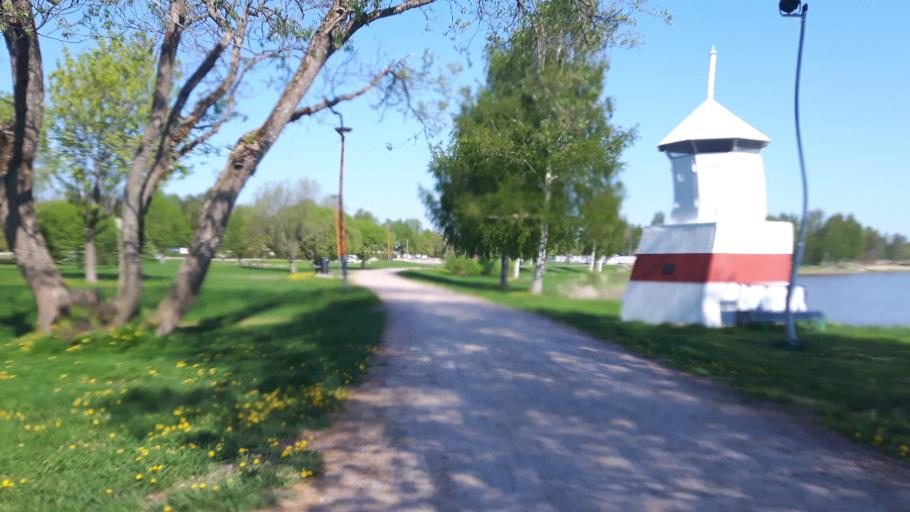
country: FI
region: Uusimaa
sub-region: Loviisa
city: Lovisa
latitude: 60.4531
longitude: 26.2344
